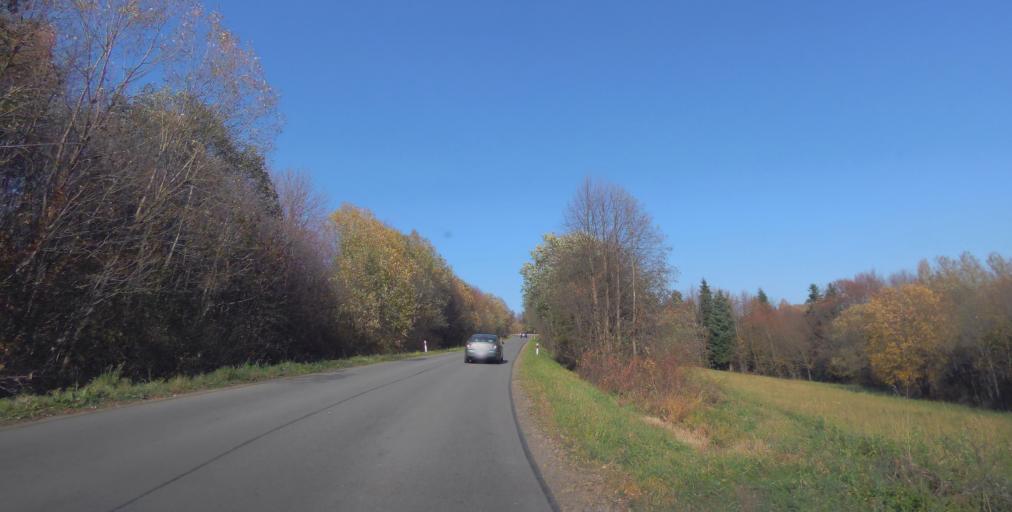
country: PL
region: Subcarpathian Voivodeship
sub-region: Powiat leski
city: Polanczyk
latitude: 49.3394
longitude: 22.4178
